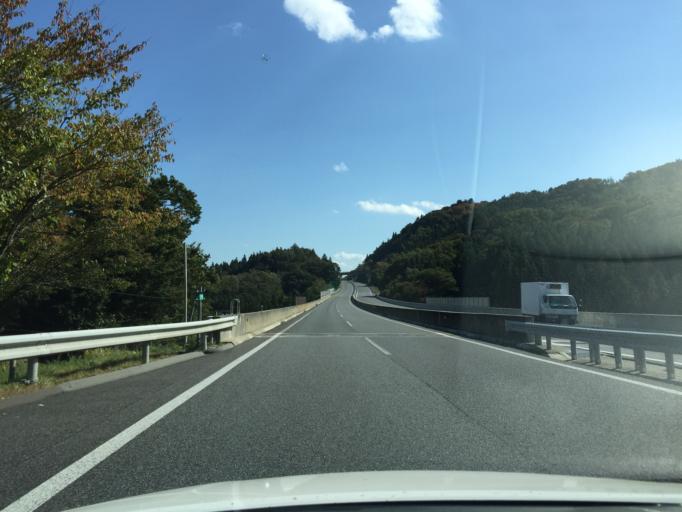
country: JP
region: Fukushima
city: Funehikimachi-funehiki
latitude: 37.2808
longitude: 140.6184
